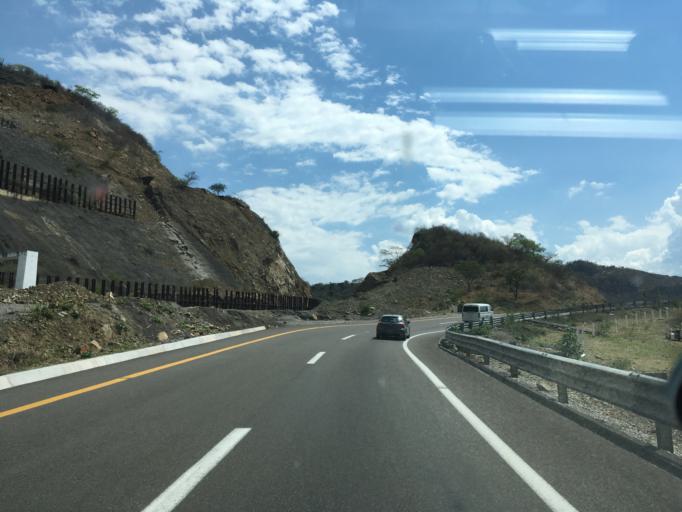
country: MX
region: Puebla
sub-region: San Jose Miahuatlan
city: San Pedro Tetitlan
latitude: 18.1122
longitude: -97.3409
